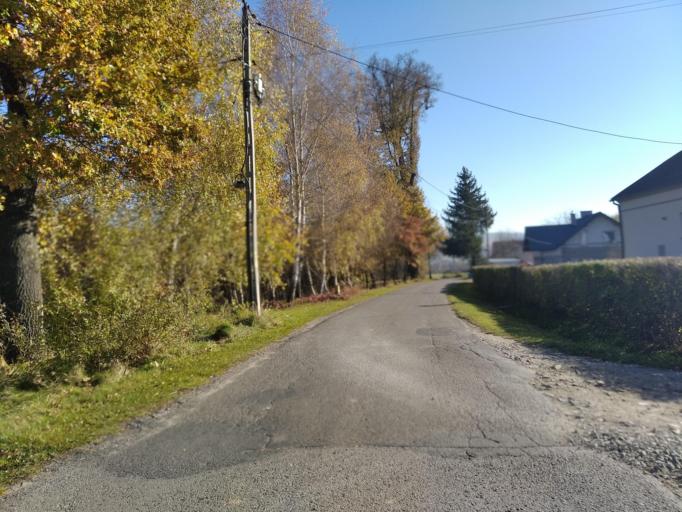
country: PL
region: Subcarpathian Voivodeship
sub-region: Powiat strzyzowski
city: Frysztak
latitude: 49.8498
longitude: 21.6101
